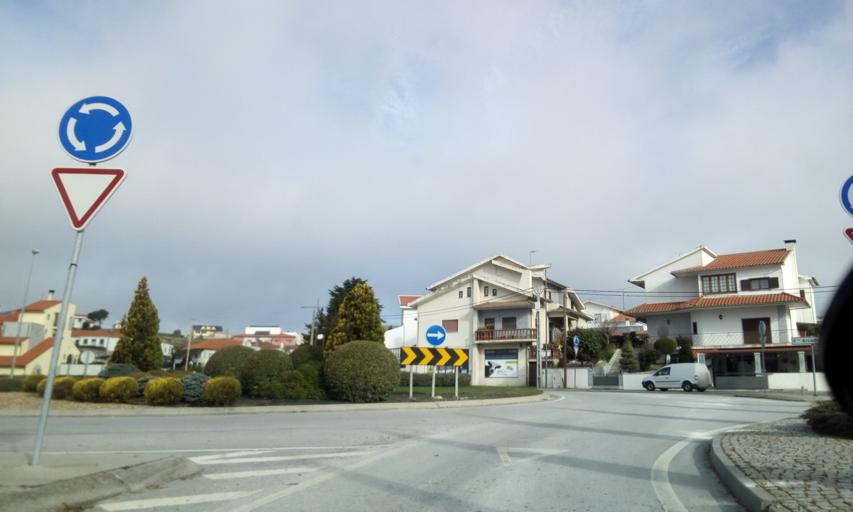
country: PT
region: Guarda
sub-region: Aguiar da Beira
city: Aguiar da Beira
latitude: 40.8177
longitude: -7.5381
